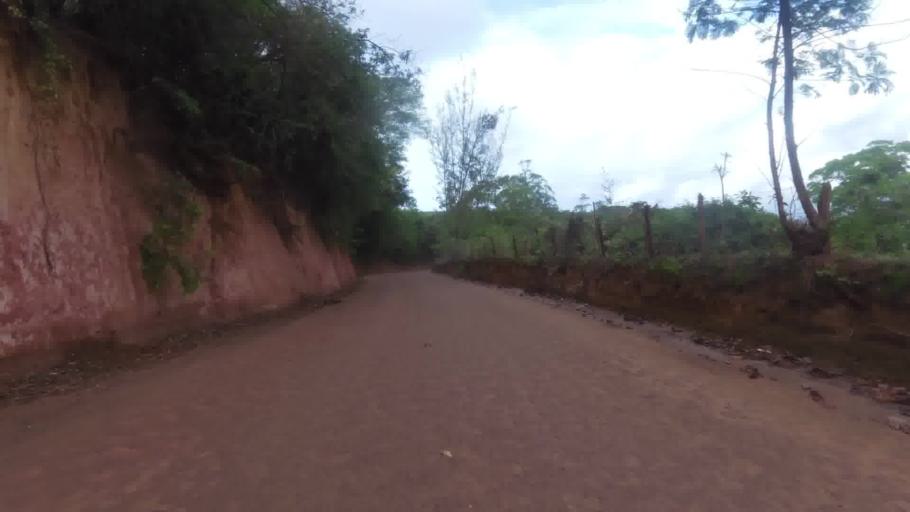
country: BR
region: Espirito Santo
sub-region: Piuma
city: Piuma
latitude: -20.7854
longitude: -40.6302
